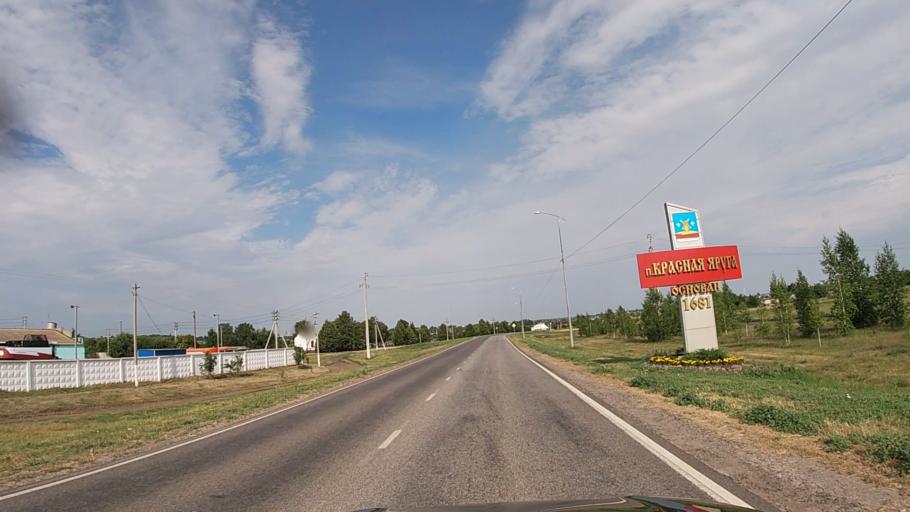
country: RU
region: Belgorod
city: Krasnaya Yaruga
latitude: 50.7983
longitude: 35.6816
